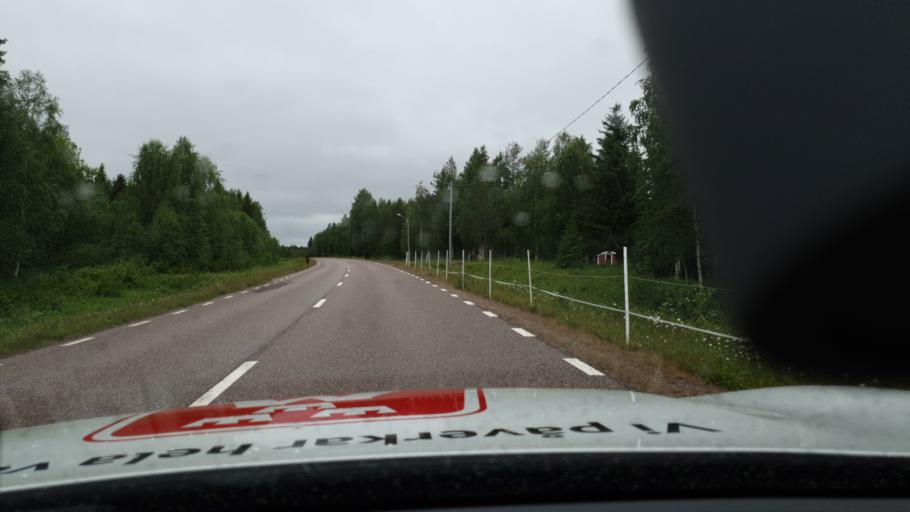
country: FI
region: Lapland
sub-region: Torniolaakso
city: Pello
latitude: 66.9571
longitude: 23.8376
